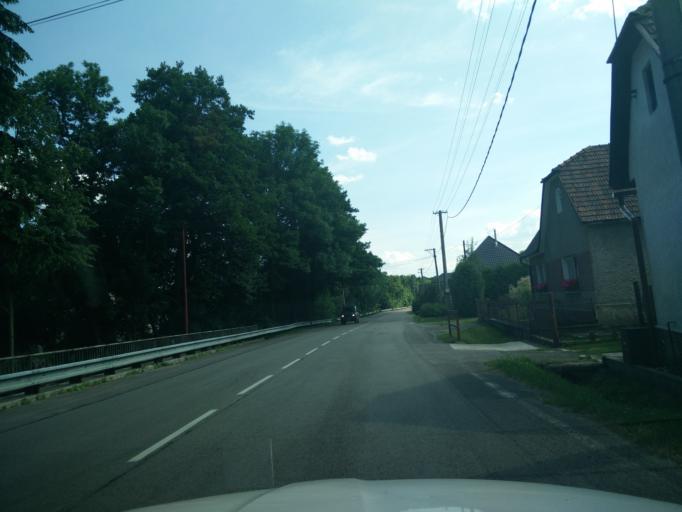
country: SK
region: Nitriansky
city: Prievidza
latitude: 48.8929
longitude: 18.6415
